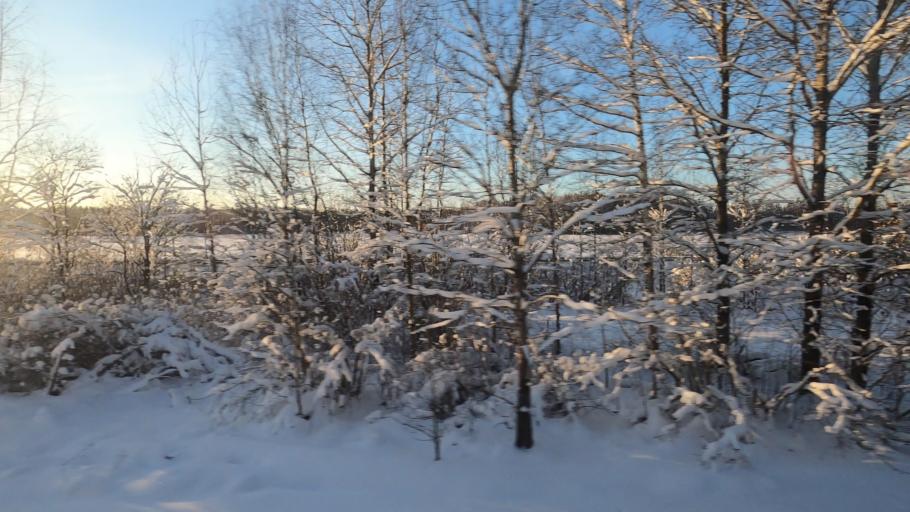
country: RU
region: Moskovskaya
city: Novo-Nikol'skoye
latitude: 56.6461
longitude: 37.5633
